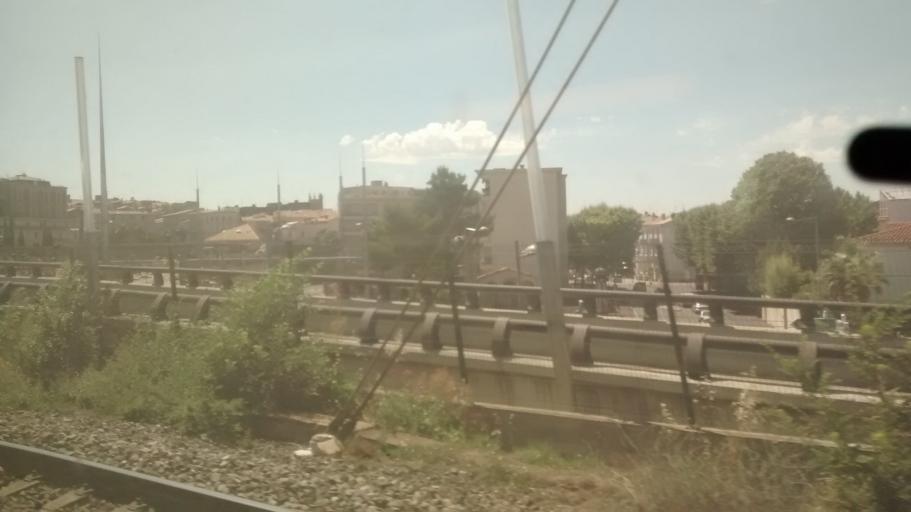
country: FR
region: Languedoc-Roussillon
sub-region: Departement de l'Herault
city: Montpellier
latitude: 43.6149
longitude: 3.8840
